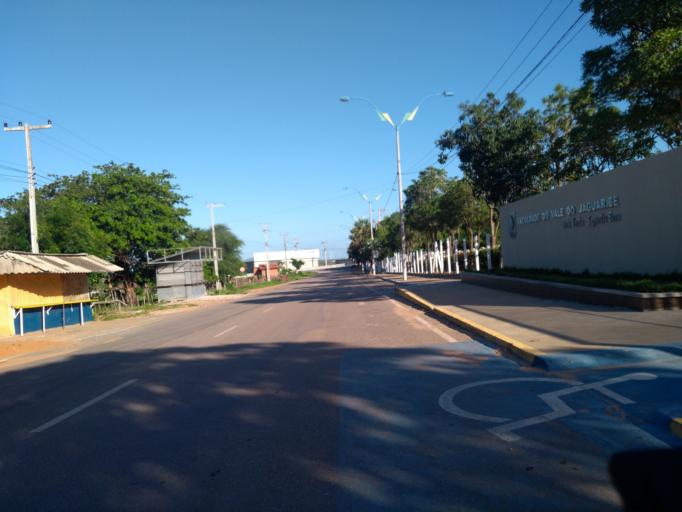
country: BR
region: Ceara
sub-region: Aracati
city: Aracati
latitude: -4.5712
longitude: -37.7931
